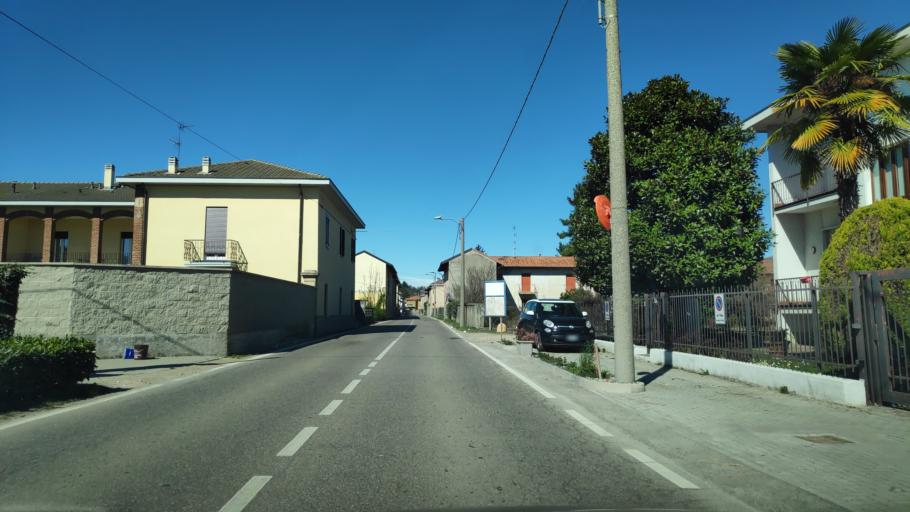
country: IT
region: Lombardy
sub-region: Provincia di Varese
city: Cassano Magnago
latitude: 45.6721
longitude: 8.8329
